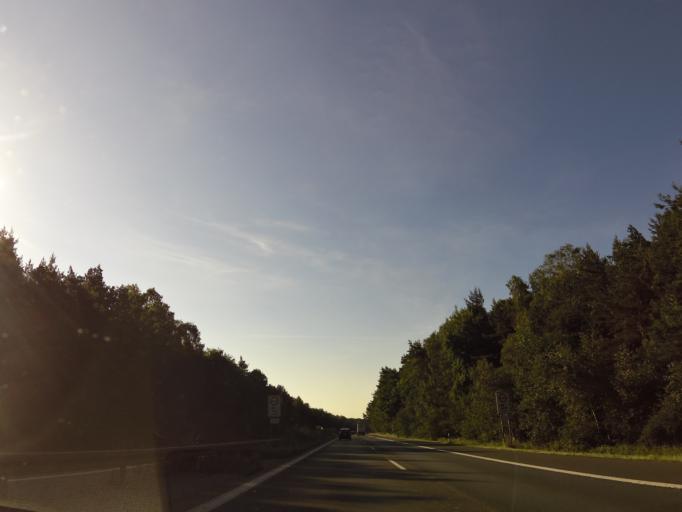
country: DE
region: Bavaria
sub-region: Regierungsbezirk Mittelfranken
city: Grossenseebach
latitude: 49.6661
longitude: 10.8841
